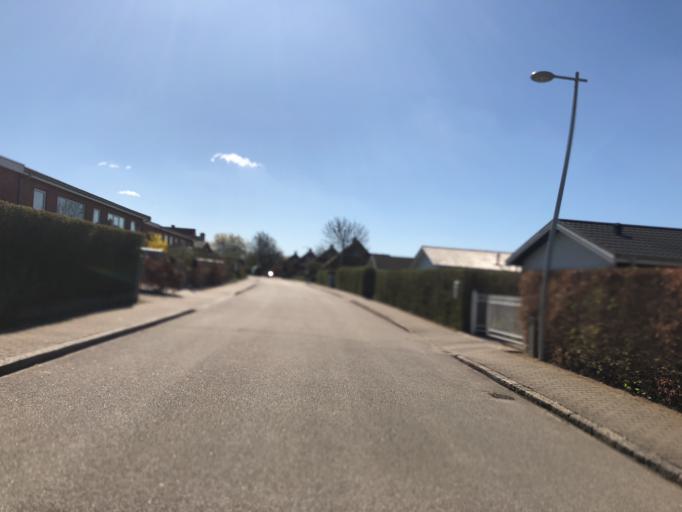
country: DK
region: Zealand
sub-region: Ringsted Kommune
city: Ringsted
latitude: 55.4358
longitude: 11.7837
